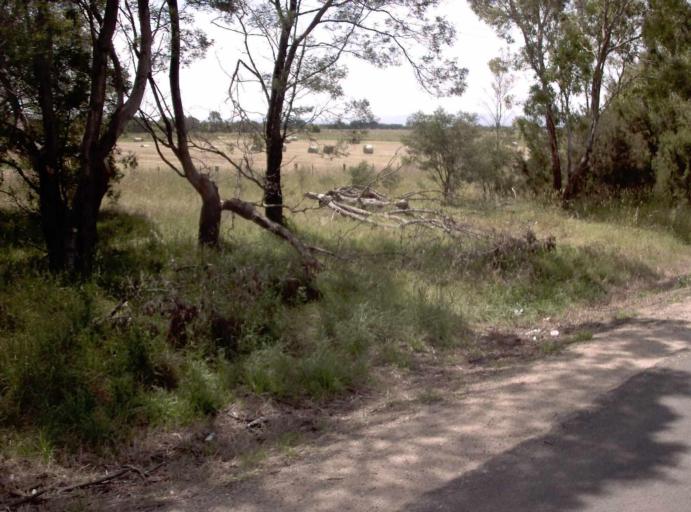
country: AU
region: Victoria
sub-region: Wellington
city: Sale
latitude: -38.0771
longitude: 147.0722
